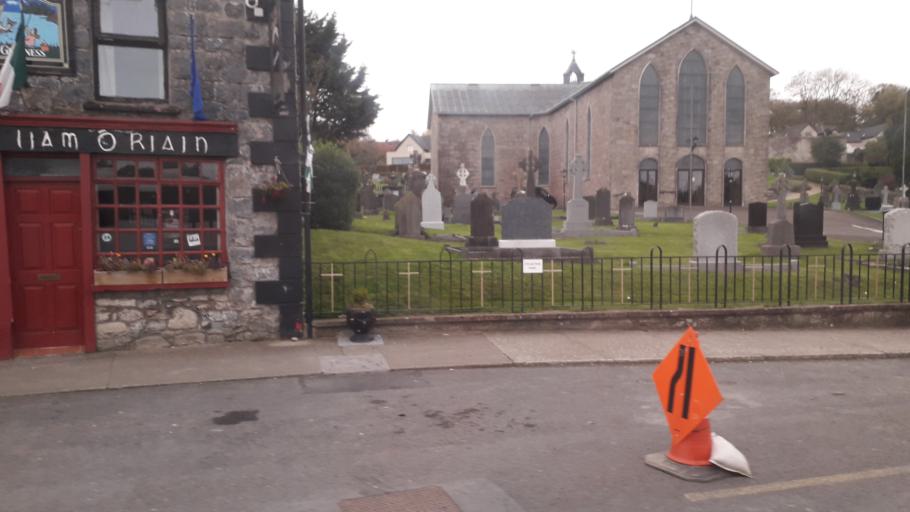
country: IE
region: Munster
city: Ballina
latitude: 52.8077
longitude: -8.4364
